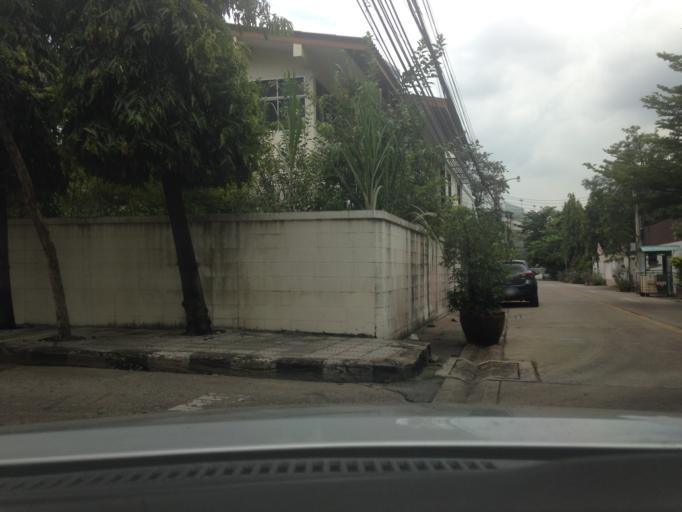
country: TH
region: Bangkok
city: Phaya Thai
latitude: 13.7852
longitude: 100.5444
